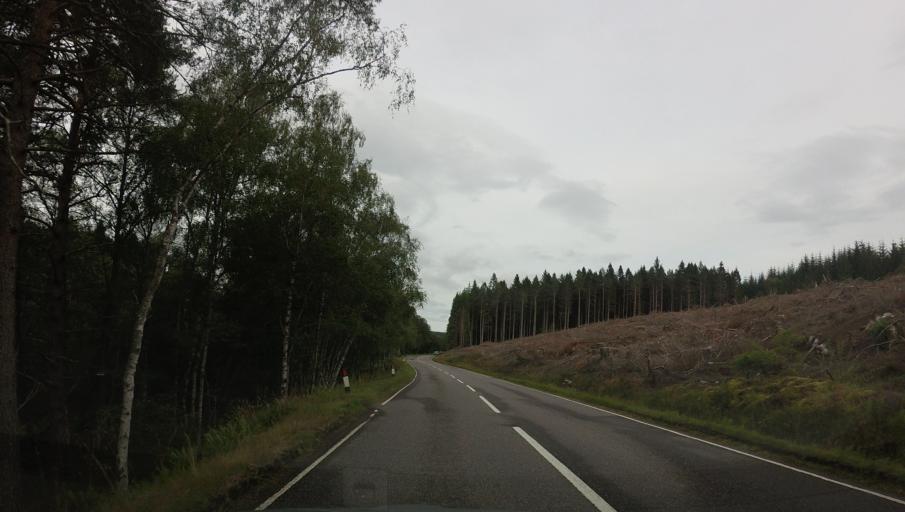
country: GB
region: Scotland
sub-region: Aberdeenshire
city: Torphins
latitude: 57.0634
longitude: -2.5990
